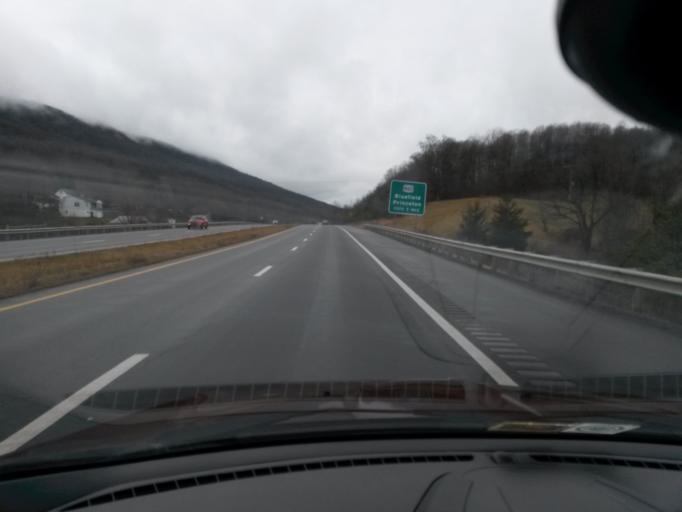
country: US
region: West Virginia
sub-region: Mercer County
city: Bluefield
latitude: 37.2800
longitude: -81.1373
